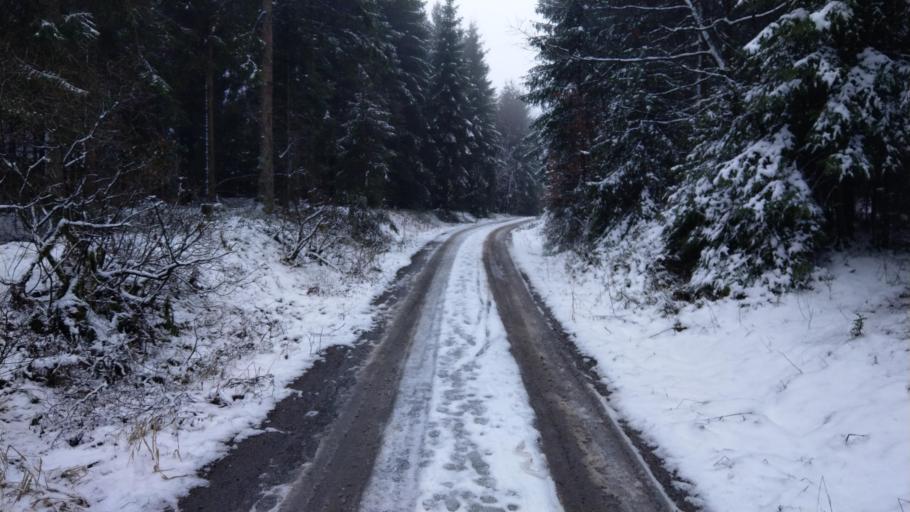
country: DE
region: North Rhine-Westphalia
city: Hilchenbach
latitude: 50.9829
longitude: 8.1644
